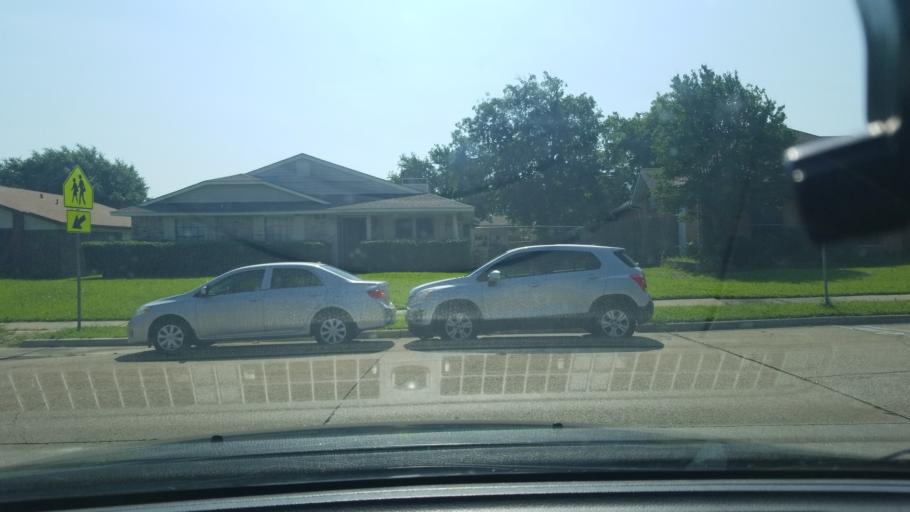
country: US
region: Texas
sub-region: Dallas County
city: Mesquite
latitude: 32.8166
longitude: -96.6182
